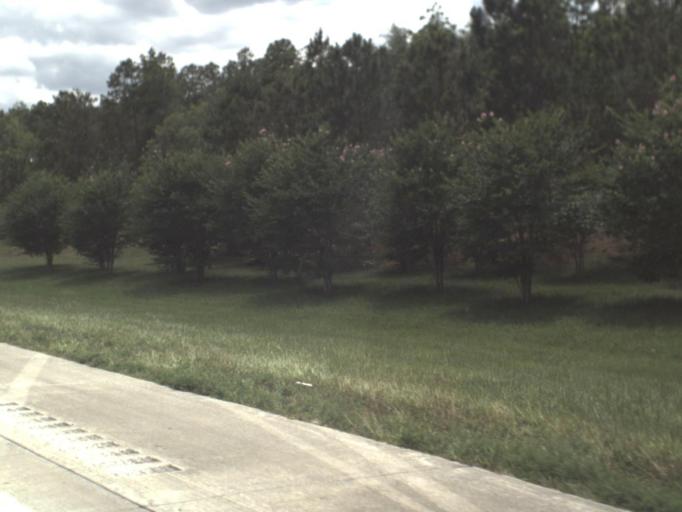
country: US
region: Florida
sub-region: Saint Johns County
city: Palm Valley
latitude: 30.2017
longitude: -81.5140
